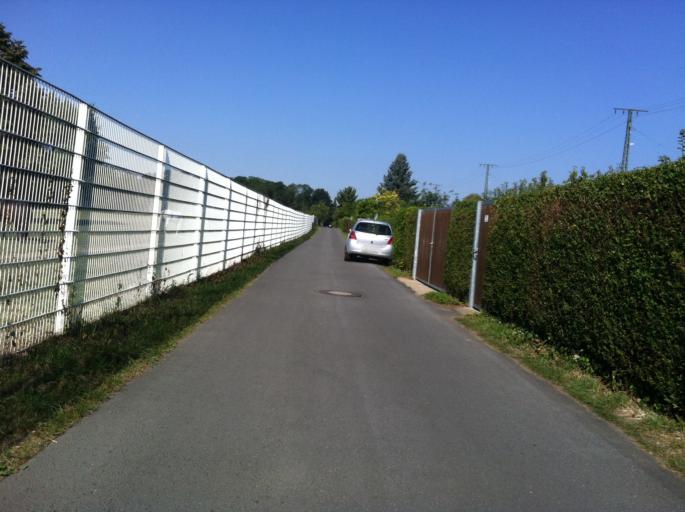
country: DE
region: North Rhine-Westphalia
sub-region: Regierungsbezirk Koln
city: Ostheim
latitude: 50.9080
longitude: 7.0282
